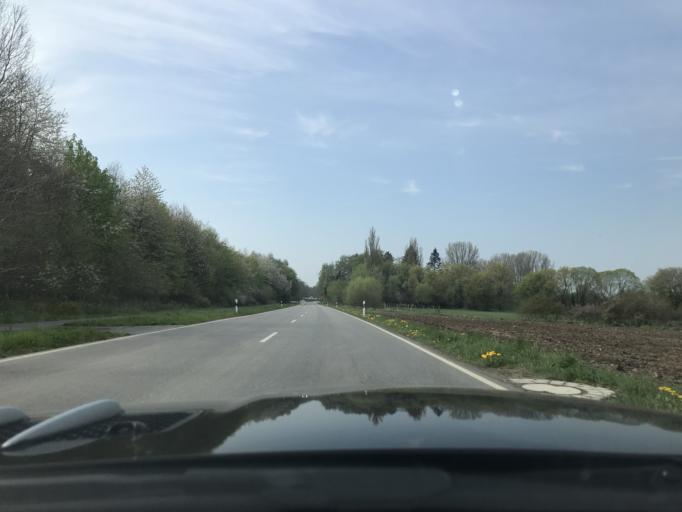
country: DE
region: Schleswig-Holstein
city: Grube
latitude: 54.2016
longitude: 11.0299
